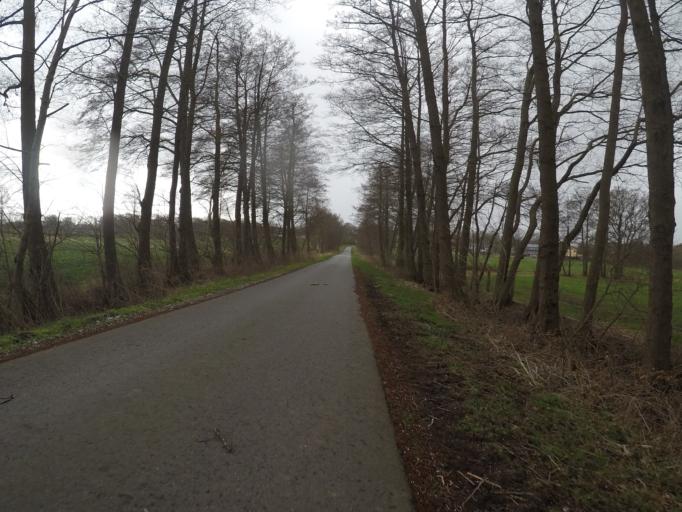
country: DE
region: Lower Saxony
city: Langen
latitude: 53.6168
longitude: 8.6397
